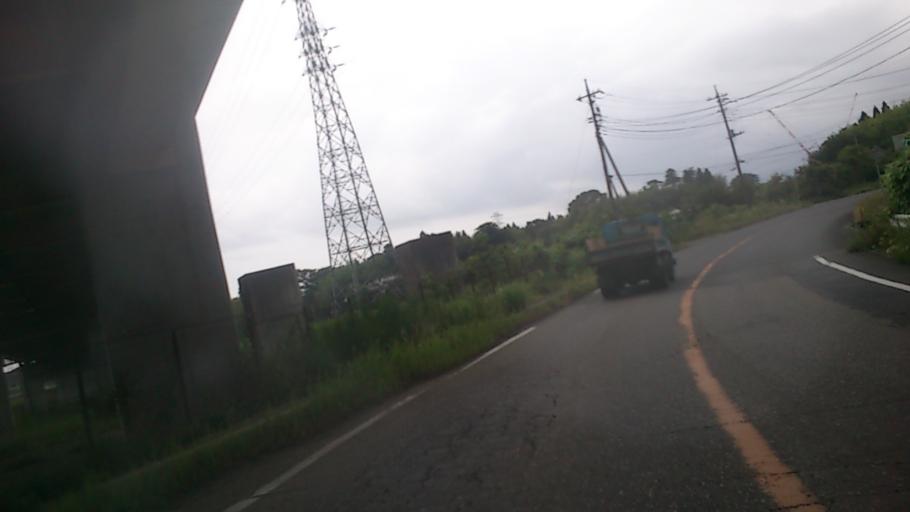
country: JP
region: Ibaraki
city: Ami
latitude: 35.9872
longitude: 140.2261
